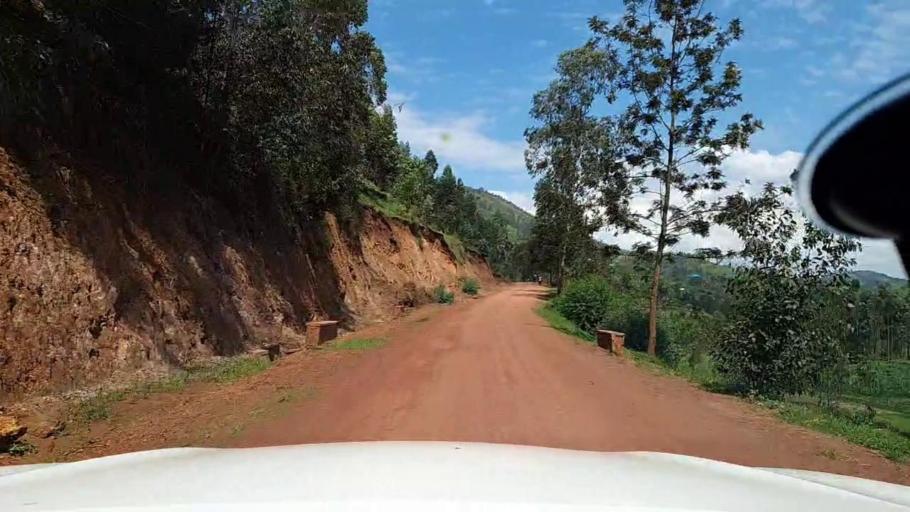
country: RW
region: Kigali
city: Kigali
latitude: -1.7793
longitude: 29.8769
